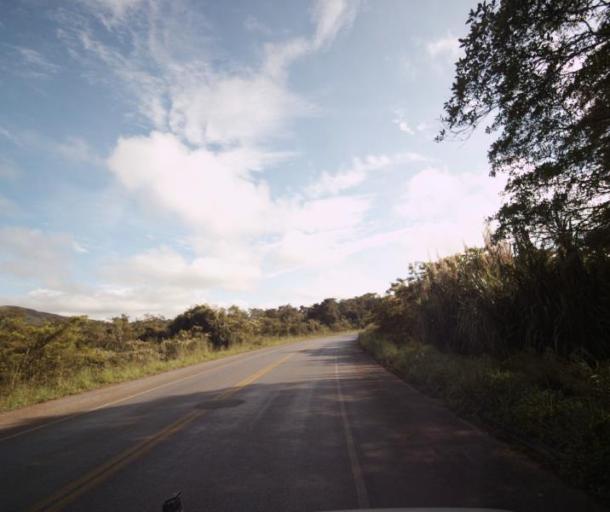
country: BR
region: Goias
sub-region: Padre Bernardo
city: Padre Bernardo
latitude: -15.4882
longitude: -48.6187
